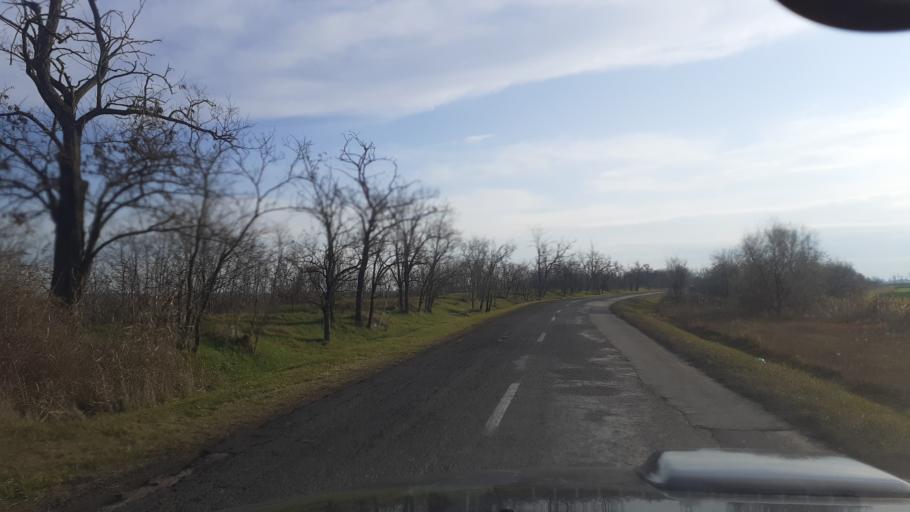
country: HU
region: Pest
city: Domsod
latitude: 47.1077
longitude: 19.0904
